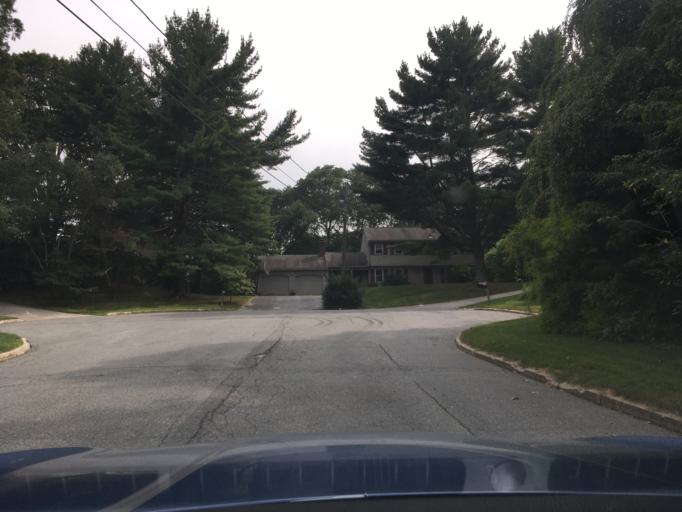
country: US
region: Rhode Island
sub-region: Kent County
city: East Greenwich
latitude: 41.6376
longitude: -71.4765
